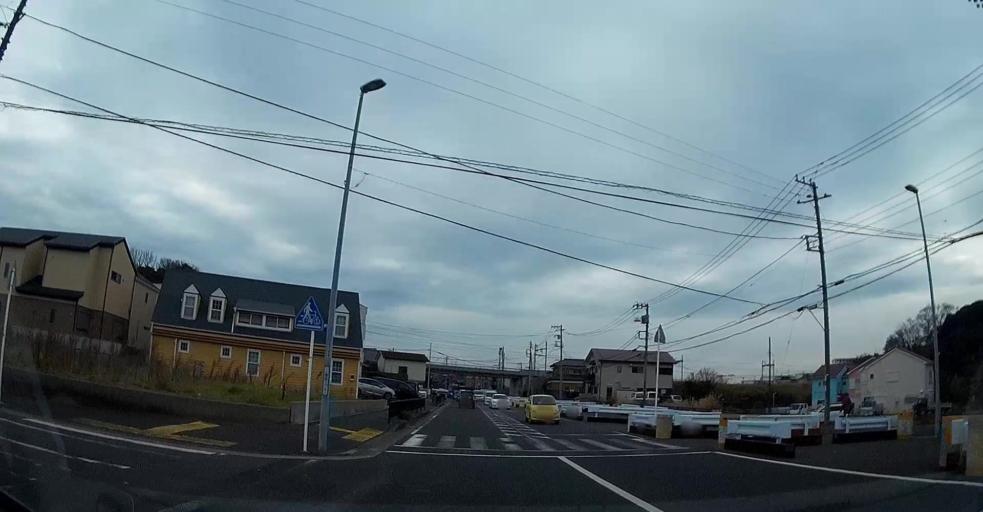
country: JP
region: Kanagawa
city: Yokosuka
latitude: 35.2083
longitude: 139.6779
